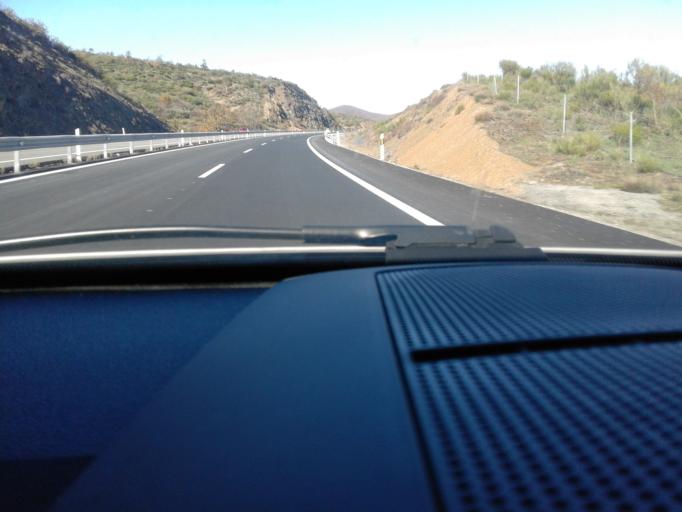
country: ES
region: Castille and Leon
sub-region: Provincia de Leon
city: Soto y Amio
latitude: 42.8008
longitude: -5.8302
